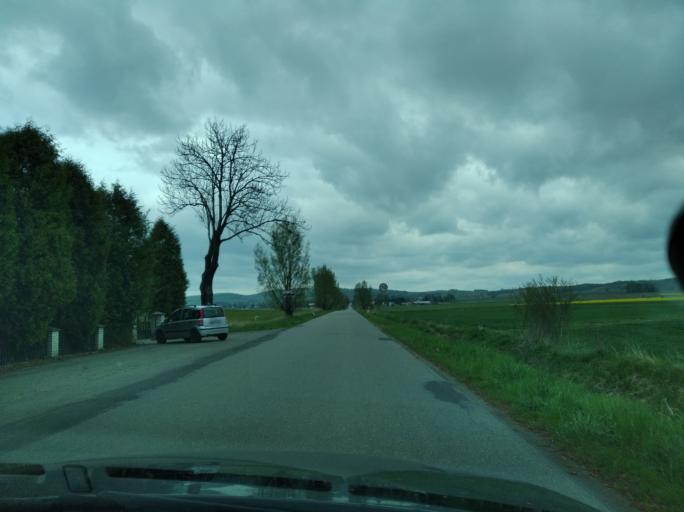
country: PL
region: Subcarpathian Voivodeship
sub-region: Powiat sanocki
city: Dlugie
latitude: 49.5843
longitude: 22.0459
